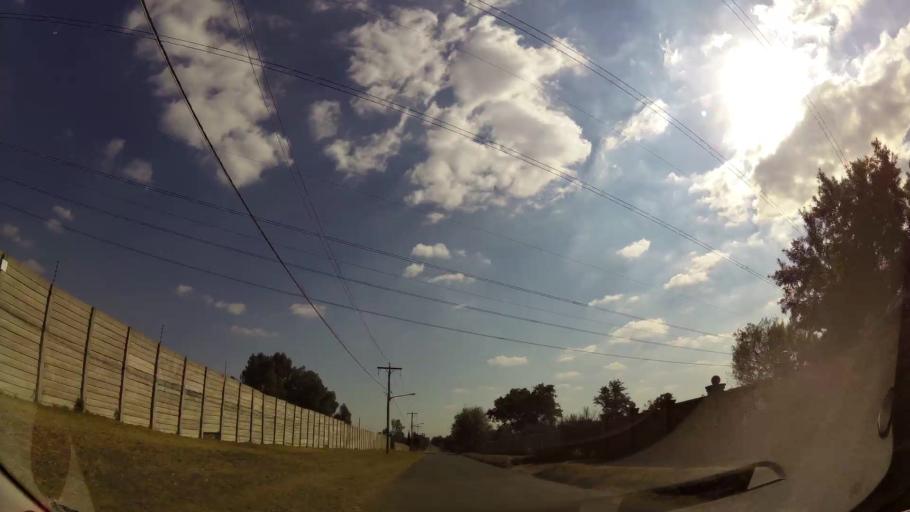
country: ZA
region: Gauteng
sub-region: Ekurhuleni Metropolitan Municipality
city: Benoni
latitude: -26.1043
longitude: 28.3544
